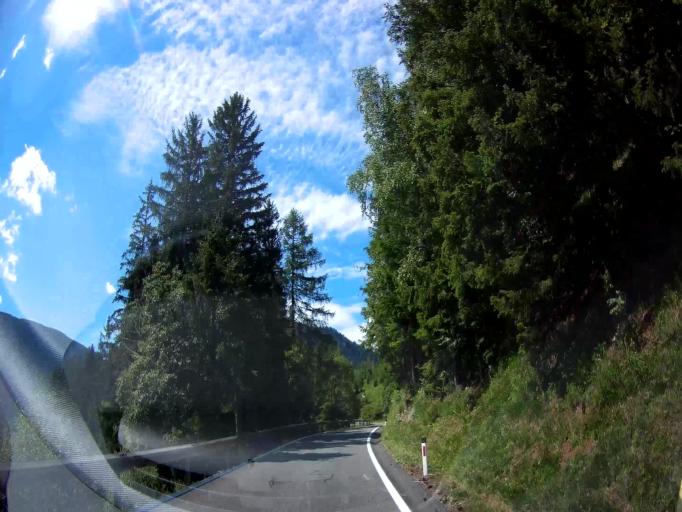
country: AT
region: Carinthia
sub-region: Politischer Bezirk Sankt Veit an der Glan
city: Glodnitz
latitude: 46.9213
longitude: 14.0562
